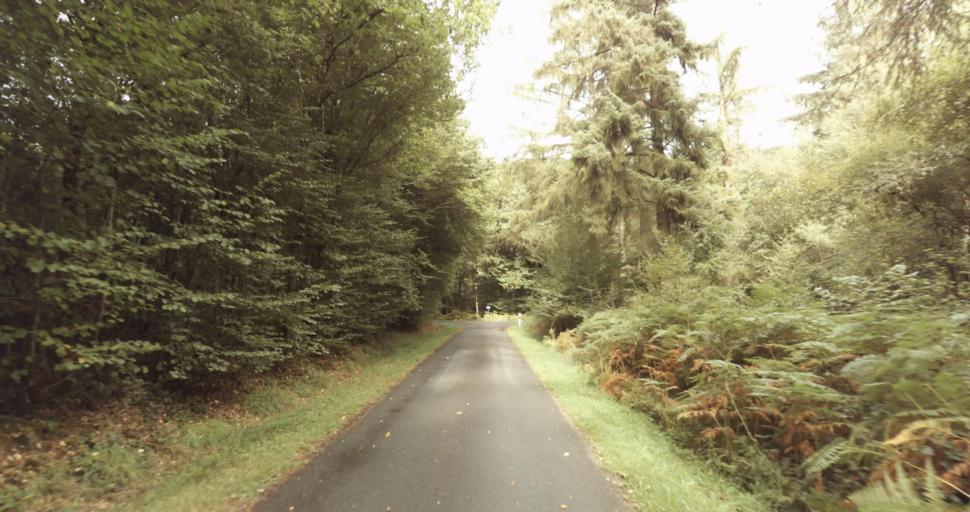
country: FR
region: Lower Normandy
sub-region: Departement de l'Orne
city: Sainte-Gauburge-Sainte-Colombe
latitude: 48.7774
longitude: 0.3893
